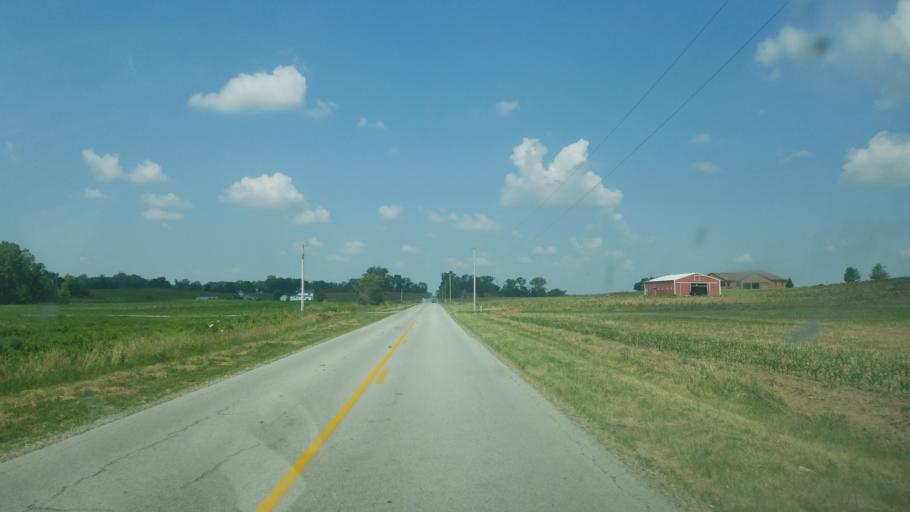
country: US
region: Ohio
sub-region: Auglaize County
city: Cridersville
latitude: 40.5709
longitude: -84.0897
